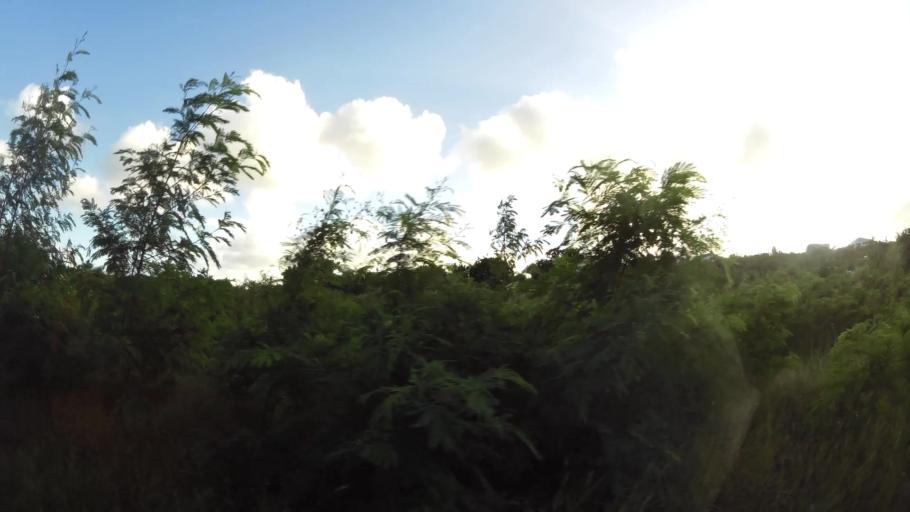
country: AG
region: Saint George
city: Piggotts
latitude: 17.1179
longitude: -61.7903
